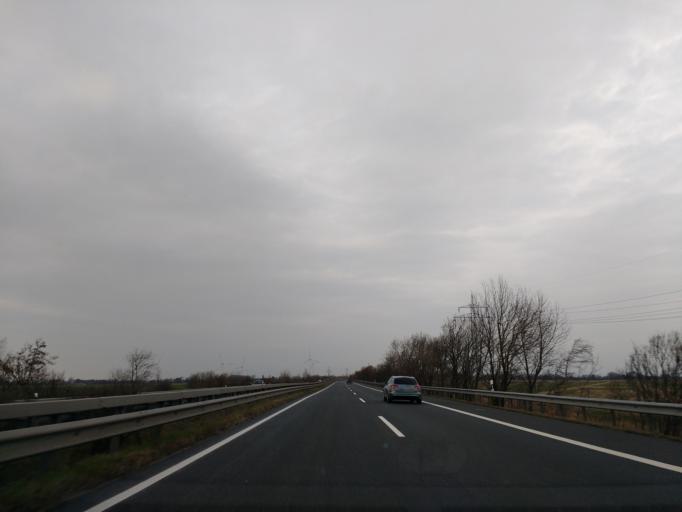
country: DE
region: Lower Saxony
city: Cuxhaven
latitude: 53.7986
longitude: 8.7077
